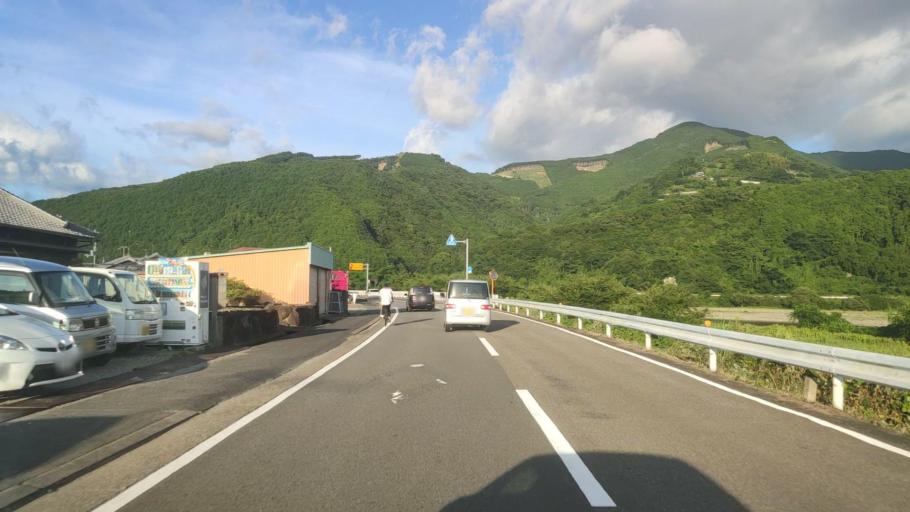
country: JP
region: Wakayama
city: Tanabe
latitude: 33.7184
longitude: 135.4791
